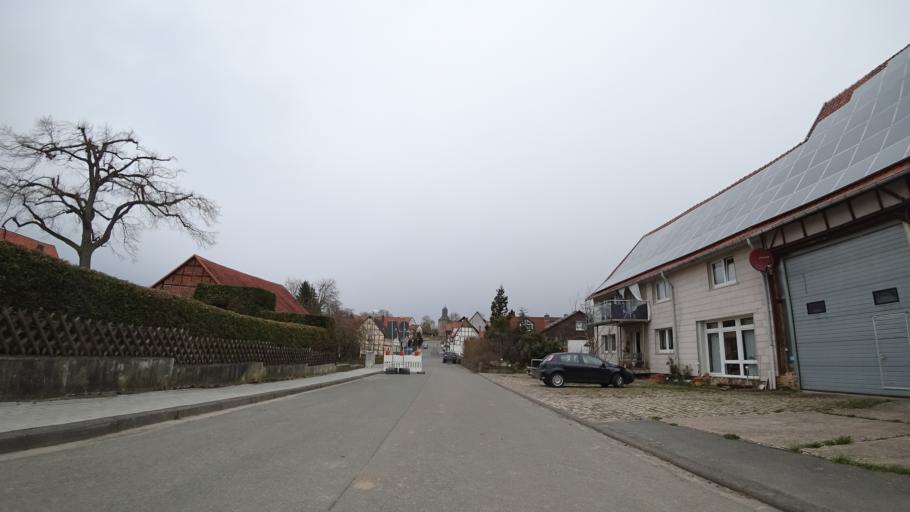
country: DE
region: Hesse
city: Grebenstein
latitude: 51.4249
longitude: 9.4341
